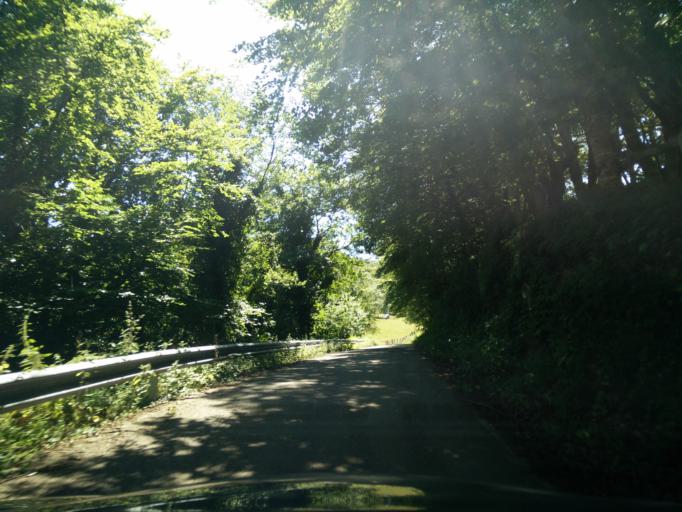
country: ES
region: Asturias
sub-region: Province of Asturias
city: Amieva
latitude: 43.1962
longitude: -5.1495
